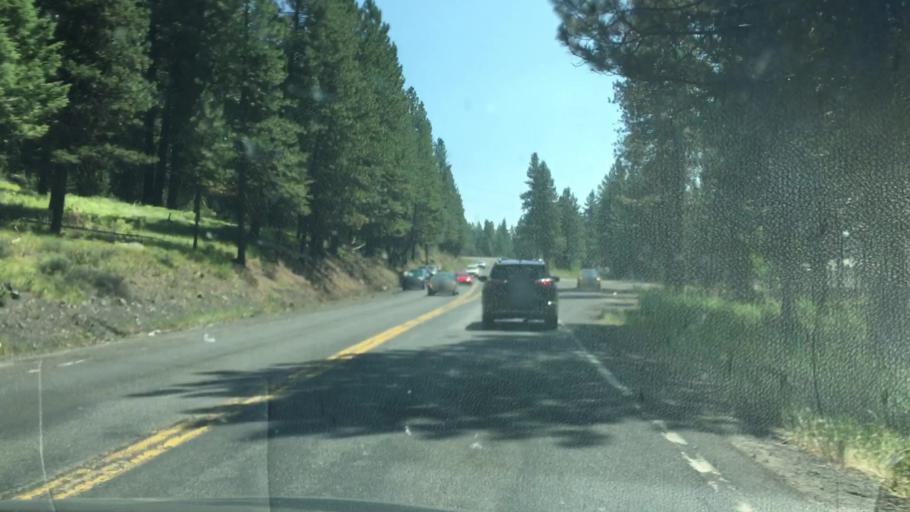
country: US
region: Idaho
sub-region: Valley County
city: McCall
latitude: 44.9350
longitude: -116.1655
